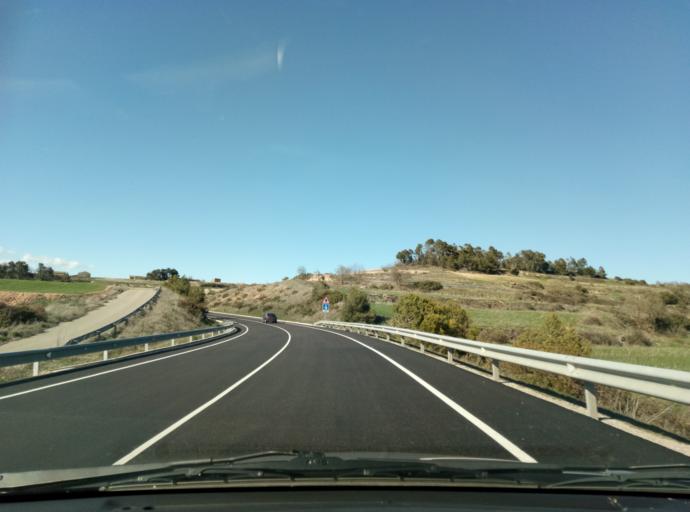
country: ES
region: Catalonia
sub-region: Provincia de Tarragona
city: Fores
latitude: 41.4947
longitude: 1.1918
